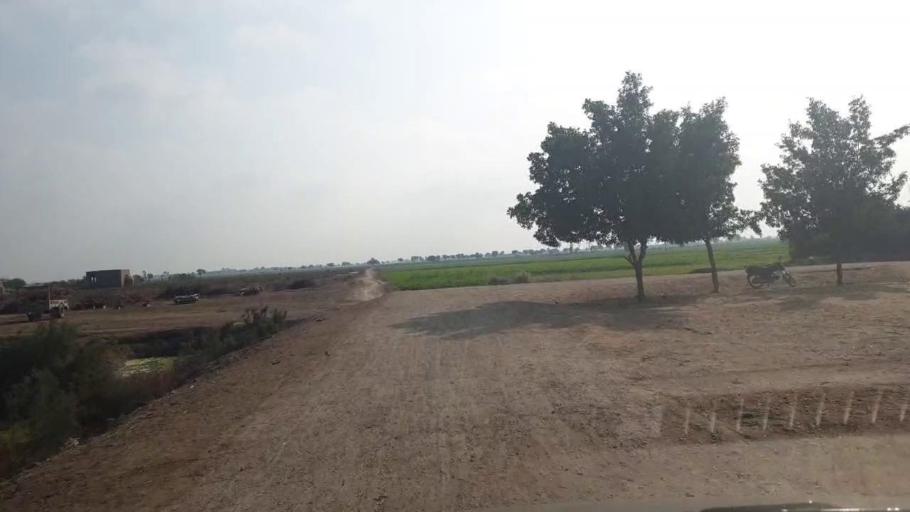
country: PK
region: Sindh
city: Shahdadpur
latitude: 25.9117
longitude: 68.6757
